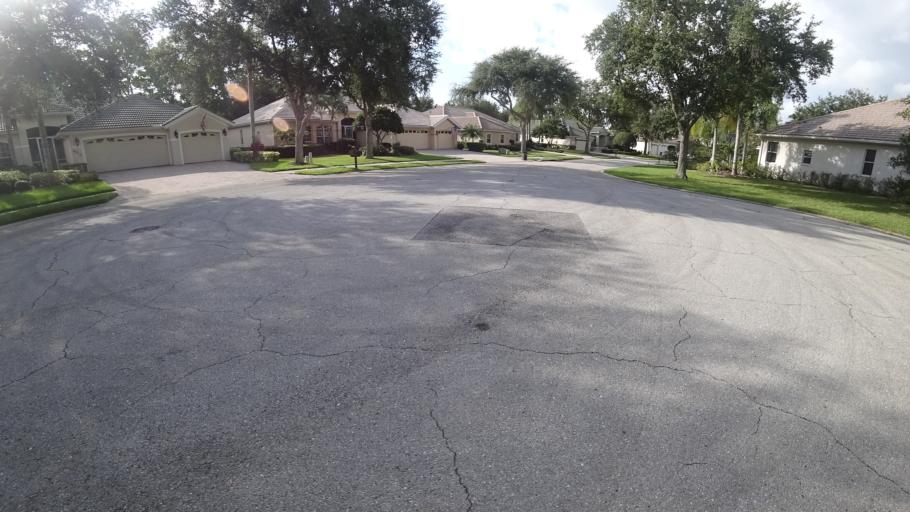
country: US
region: Florida
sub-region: Sarasota County
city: Desoto Lakes
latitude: 27.4161
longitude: -82.4727
